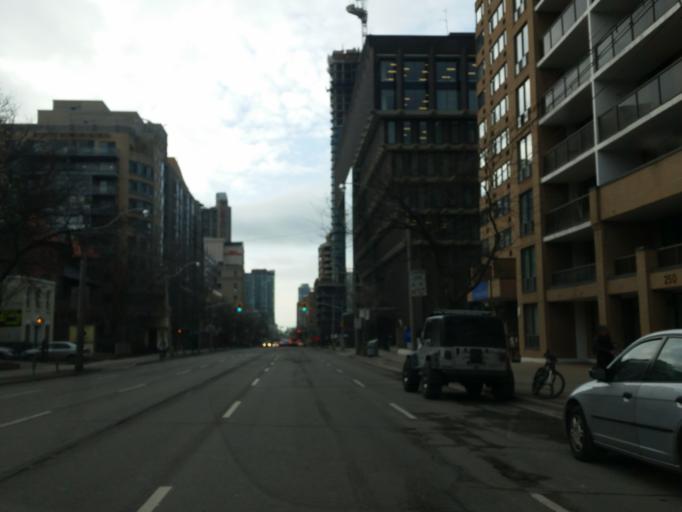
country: CA
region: Ontario
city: Toronto
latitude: 43.6593
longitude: -79.3755
